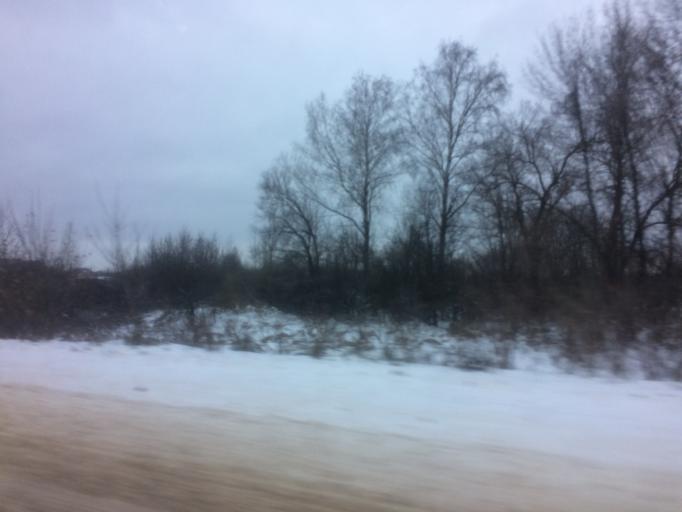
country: RU
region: Tula
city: Tula
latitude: 54.1476
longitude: 37.6446
